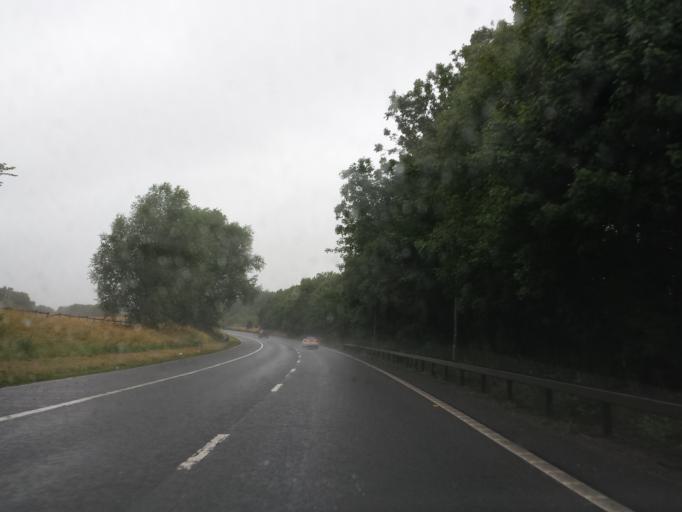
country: GB
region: England
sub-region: Leicestershire
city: Enderby
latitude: 52.6007
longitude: -1.2026
